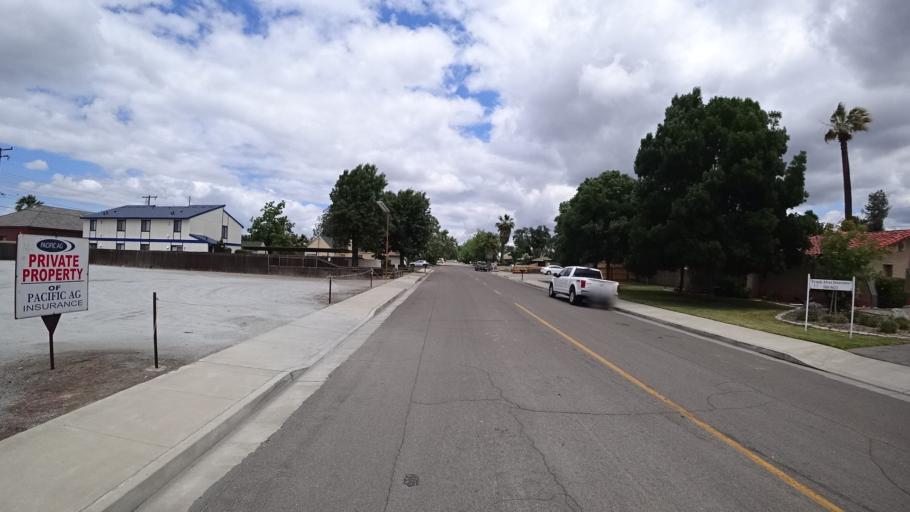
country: US
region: California
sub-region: Kings County
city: Hanford
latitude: 36.3428
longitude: -119.6540
